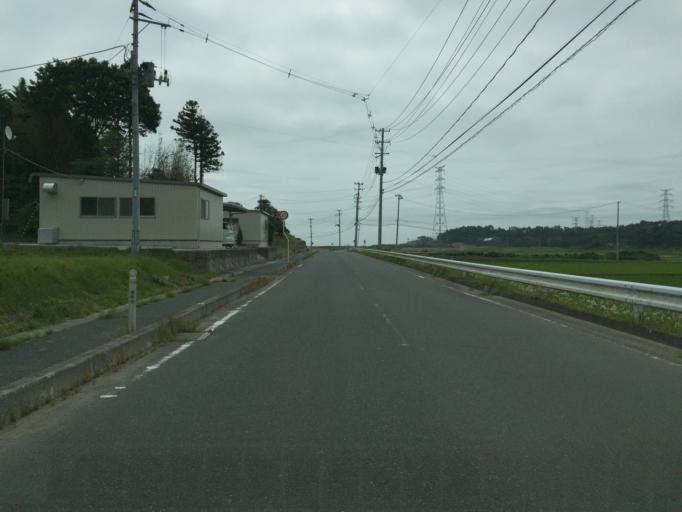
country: JP
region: Fukushima
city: Namie
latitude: 37.6645
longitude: 141.0099
